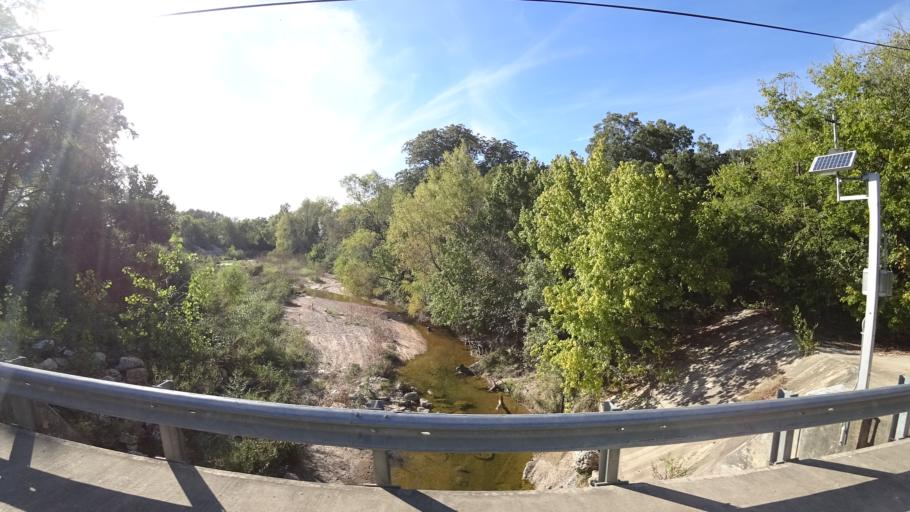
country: US
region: Texas
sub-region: Travis County
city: Austin
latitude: 30.2627
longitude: -97.6685
